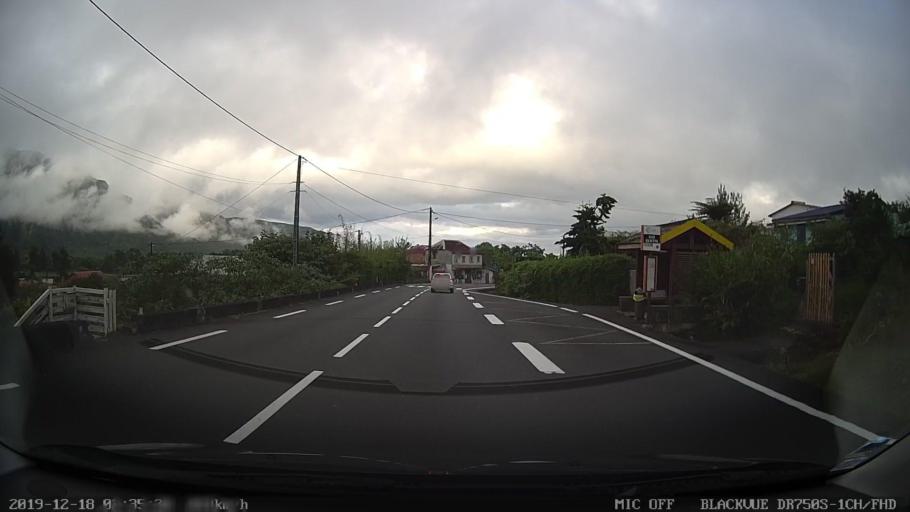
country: RE
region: Reunion
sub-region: Reunion
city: Salazie
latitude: -21.1475
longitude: 55.6162
